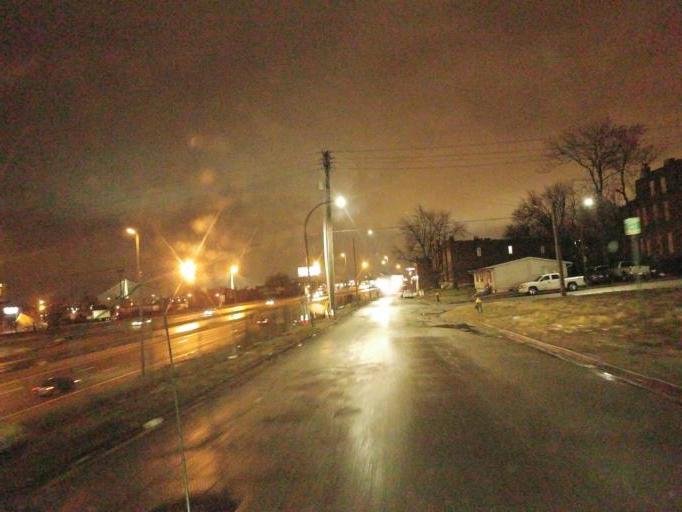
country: US
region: Illinois
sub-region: Madison County
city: Venice
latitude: 38.6612
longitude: -90.1976
